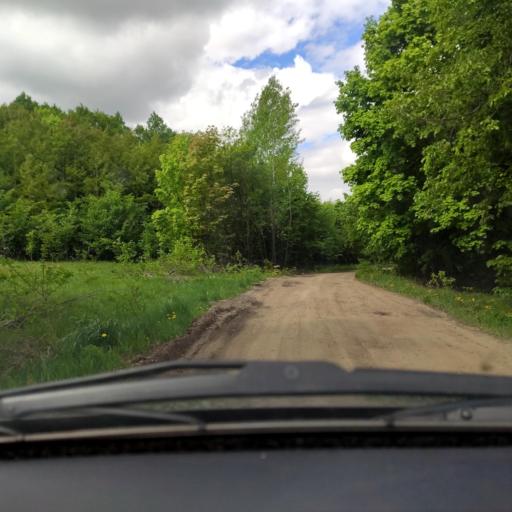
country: RU
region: Bashkortostan
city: Kabakovo
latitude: 54.7056
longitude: 56.1633
